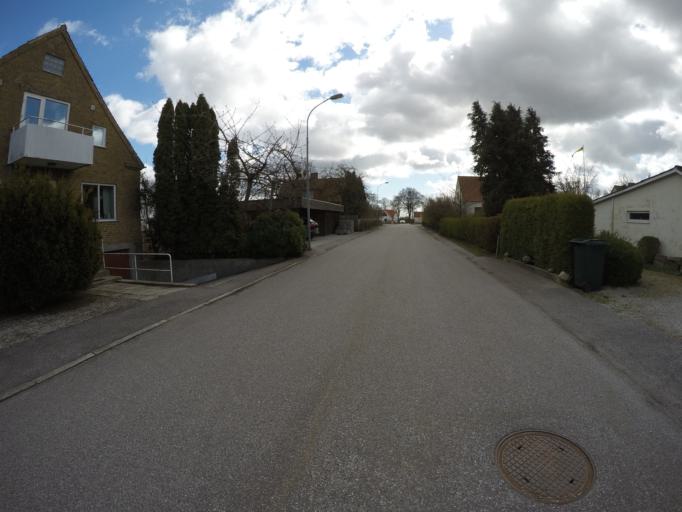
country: SE
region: Skane
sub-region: Ystads Kommun
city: Kopingebro
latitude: 55.4419
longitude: 14.1158
